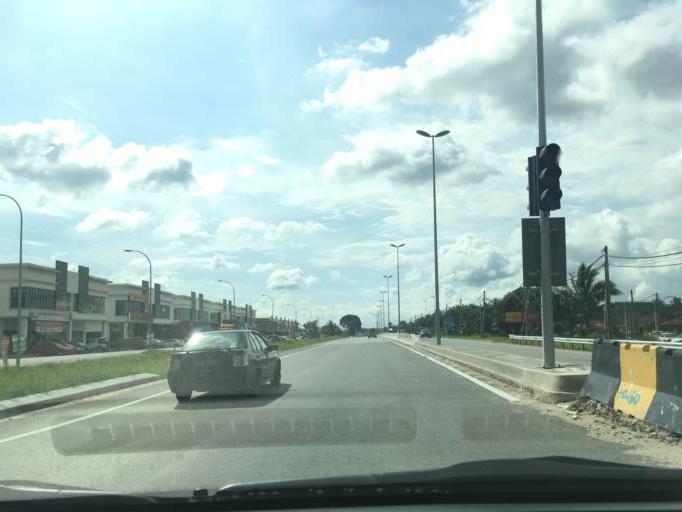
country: MY
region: Selangor
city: Batu Arang
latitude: 3.3104
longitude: 101.4220
